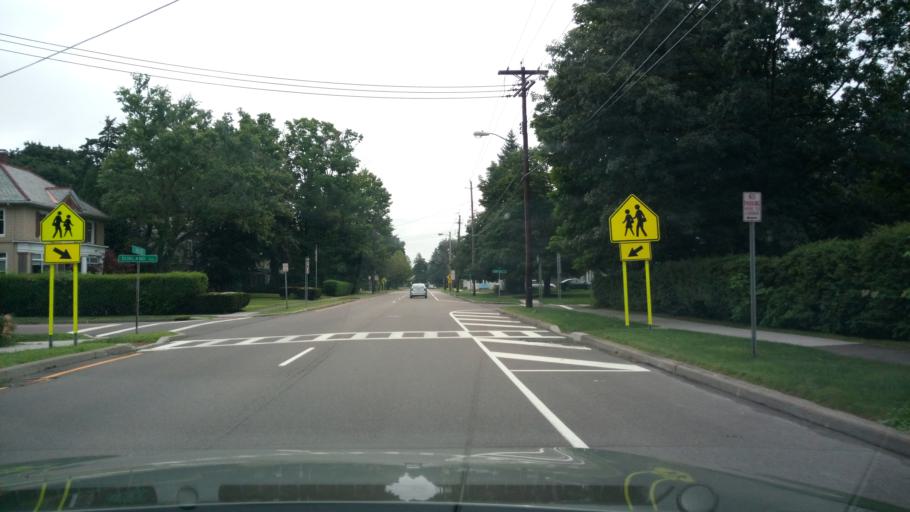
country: US
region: New York
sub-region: Chemung County
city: West Elmira
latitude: 42.0780
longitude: -76.8441
